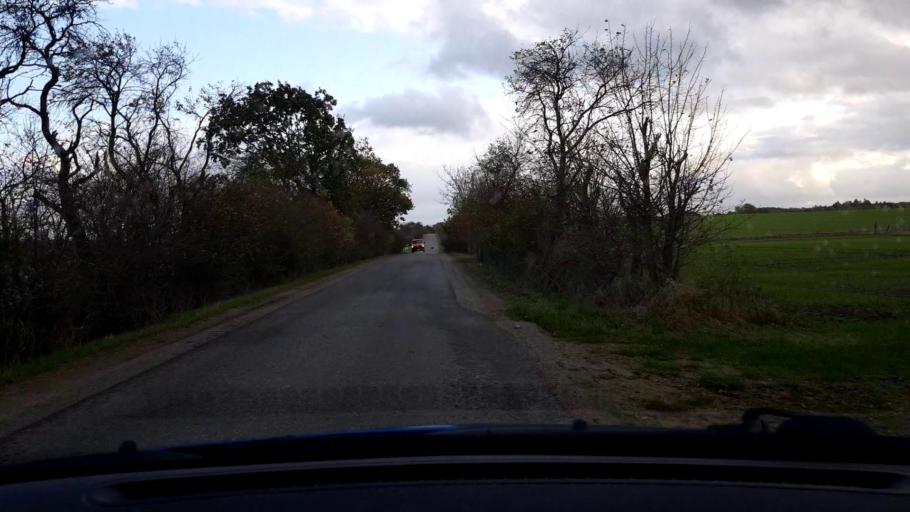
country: DE
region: Lower Saxony
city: Reinstorf
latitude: 53.2478
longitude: 10.5731
